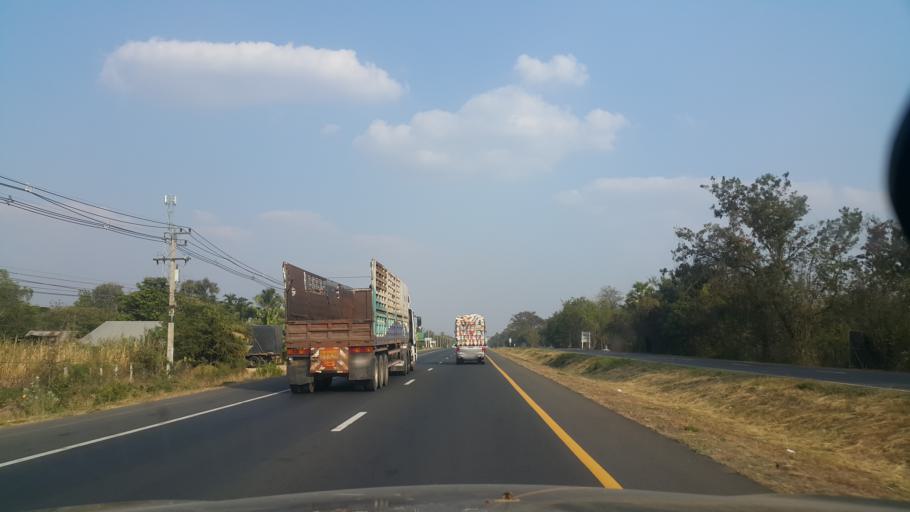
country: TH
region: Buriram
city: Nang Rong
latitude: 14.6260
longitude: 102.8618
